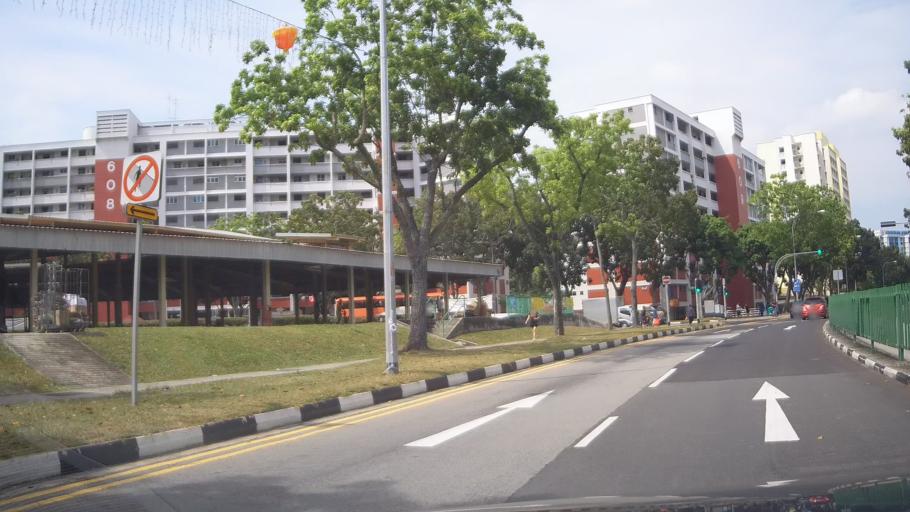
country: SG
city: Singapore
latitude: 1.3329
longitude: 103.9134
